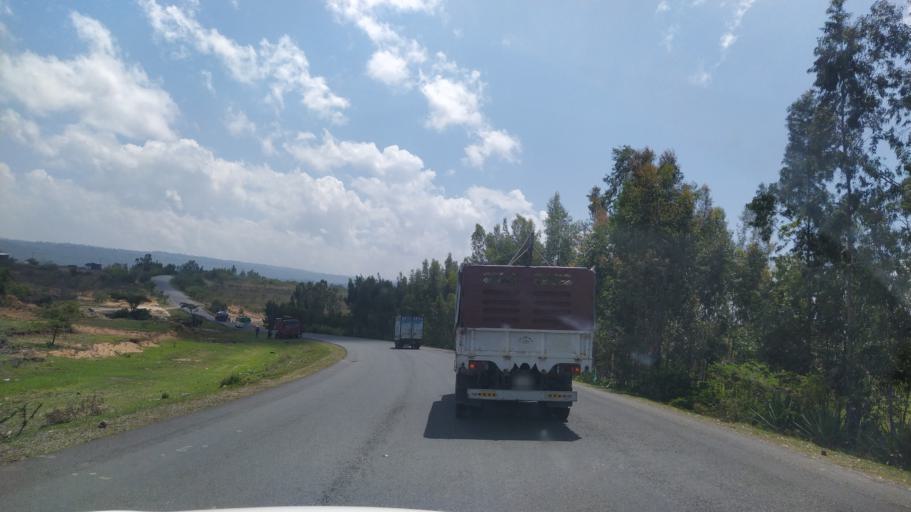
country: ET
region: Southern Nations, Nationalities, and People's Region
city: Butajira
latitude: 7.7730
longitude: 38.1395
